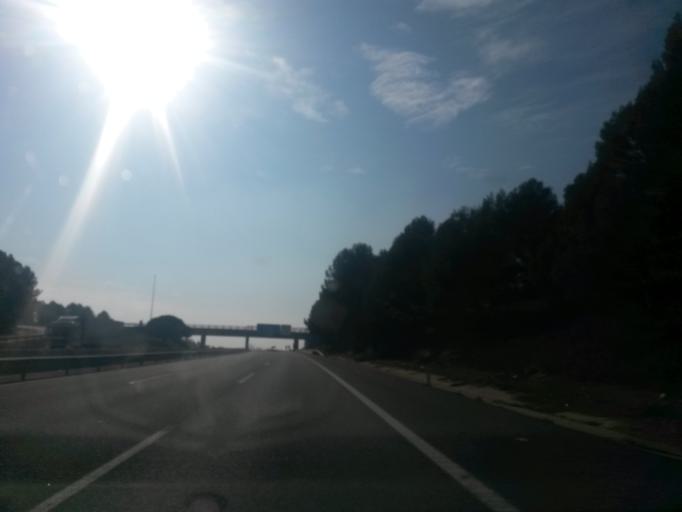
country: ES
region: Catalonia
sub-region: Provincia de Girona
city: Vilademuls
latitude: 42.1324
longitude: 2.9140
